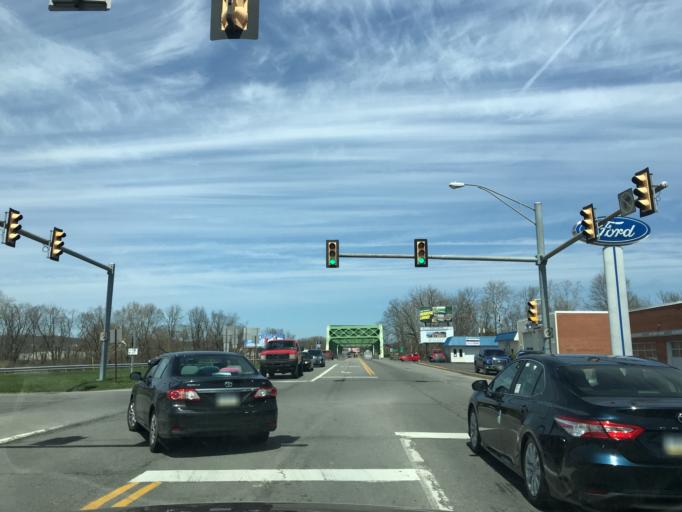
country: US
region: Pennsylvania
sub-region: Snyder County
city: Selinsgrove
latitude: 40.8118
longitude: -76.8560
